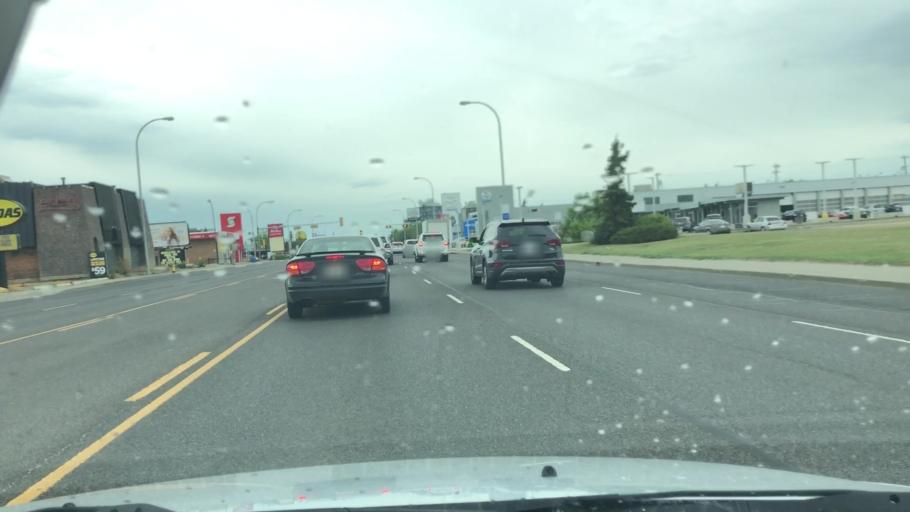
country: CA
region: Alberta
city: Edmonton
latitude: 53.5905
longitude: -113.4919
